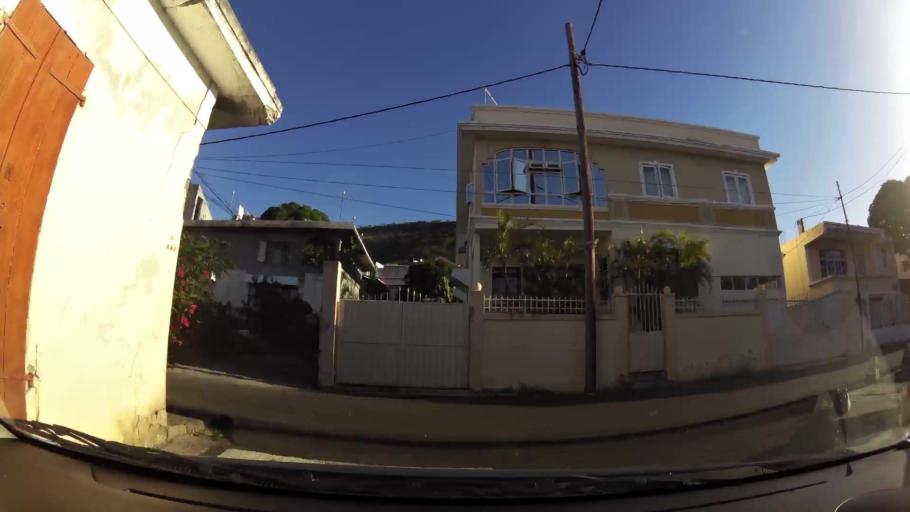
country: MU
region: Port Louis
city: Port Louis
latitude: -20.1680
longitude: 57.4966
